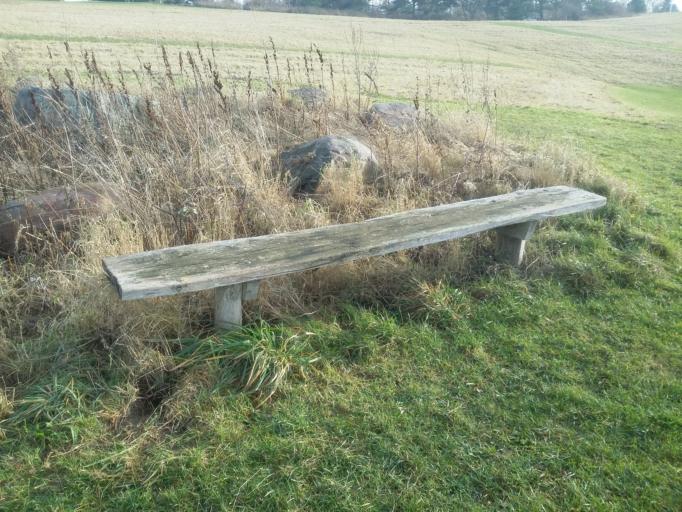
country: DK
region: Zealand
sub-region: Lejre Kommune
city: Ejby
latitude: 55.7464
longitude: 11.8565
